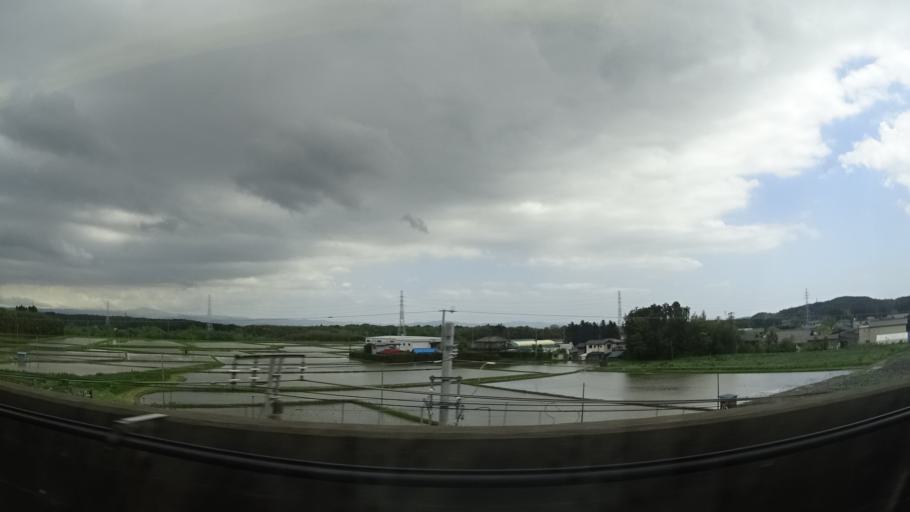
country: JP
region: Tochigi
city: Otawara
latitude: 36.9078
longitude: 140.0033
